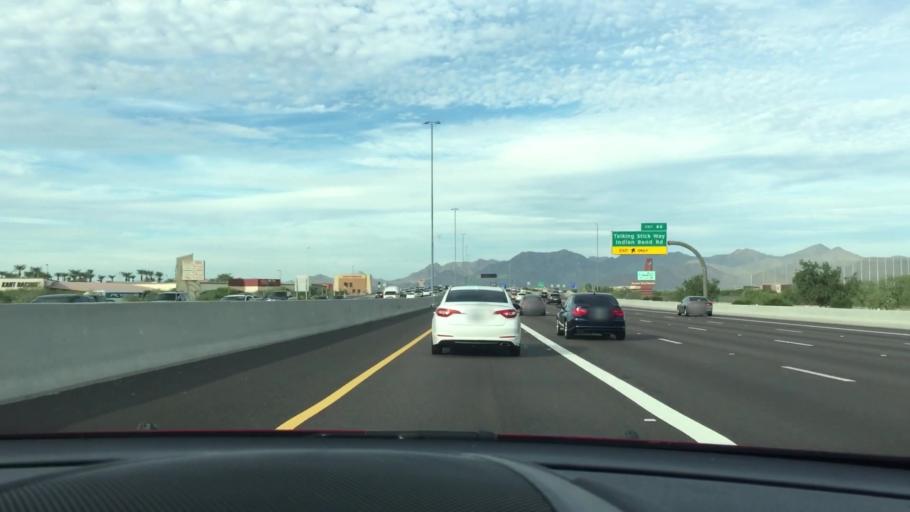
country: US
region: Arizona
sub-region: Maricopa County
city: Scottsdale
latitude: 33.5315
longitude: -111.8869
